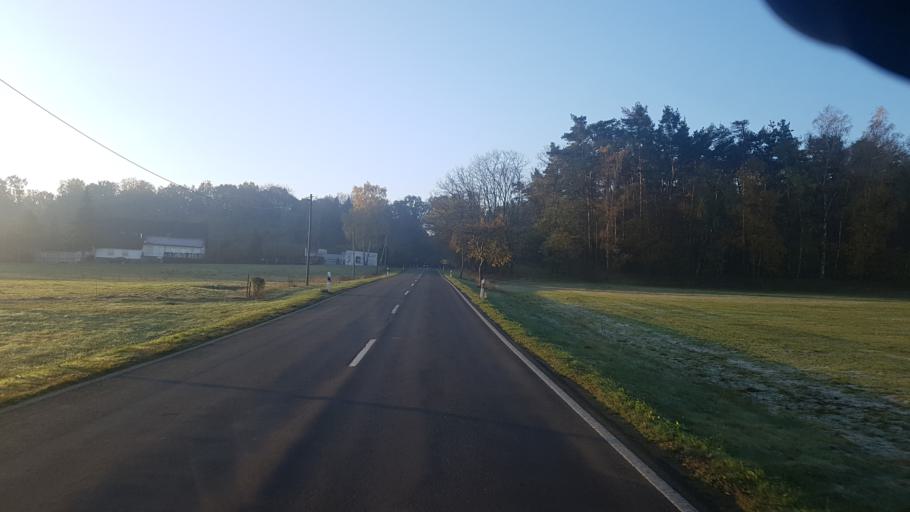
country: DE
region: Saxony
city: Schildau
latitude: 51.4285
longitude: 12.9714
